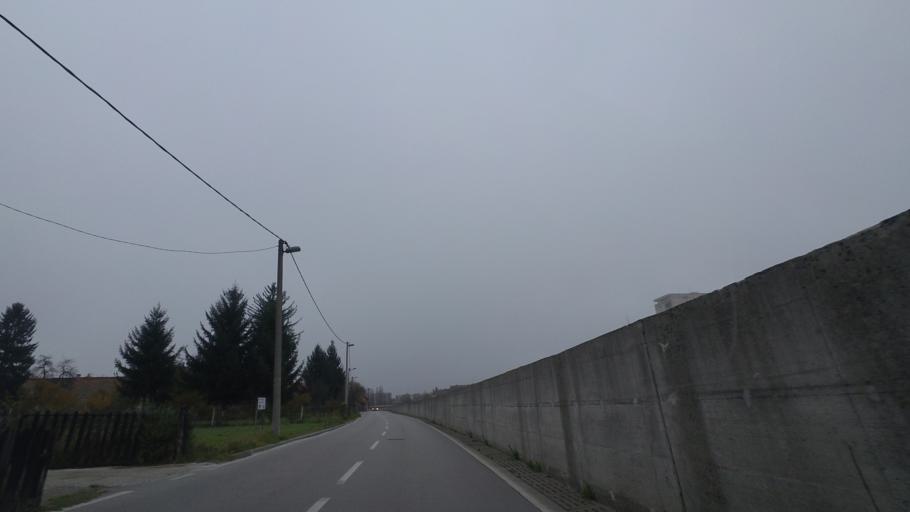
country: HR
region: Karlovacka
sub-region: Grad Karlovac
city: Karlovac
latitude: 45.4950
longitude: 15.5486
